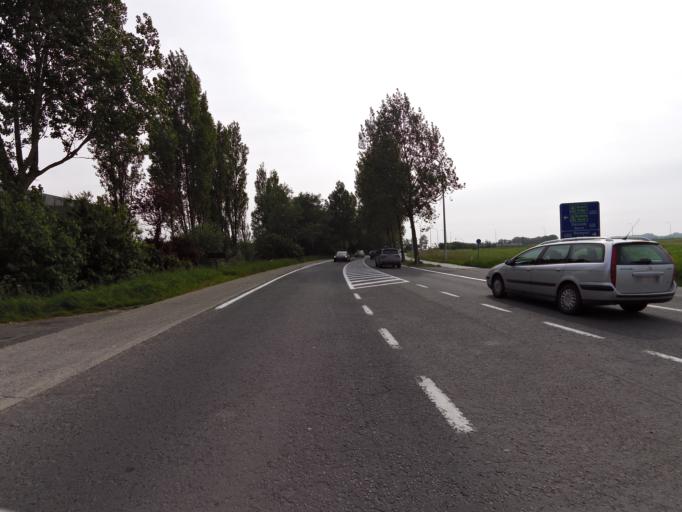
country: BE
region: Flanders
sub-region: Provincie West-Vlaanderen
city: Nieuwpoort
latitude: 51.1240
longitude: 2.7468
